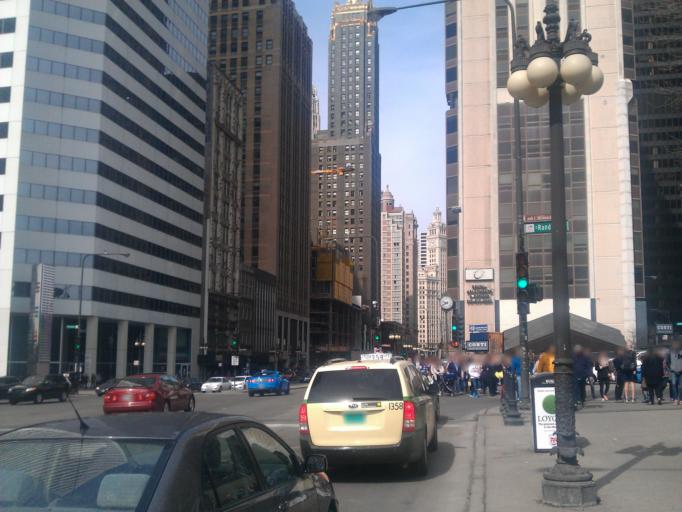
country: US
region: Illinois
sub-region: Cook County
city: Chicago
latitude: 41.8840
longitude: -87.6242
